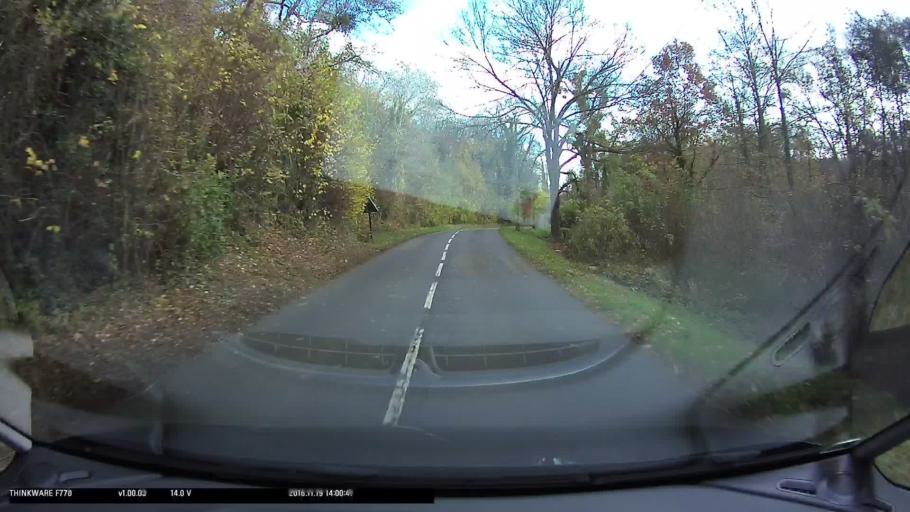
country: FR
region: Ile-de-France
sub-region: Departement du Val-d'Oise
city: Ableiges
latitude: 49.0862
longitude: 1.9975
